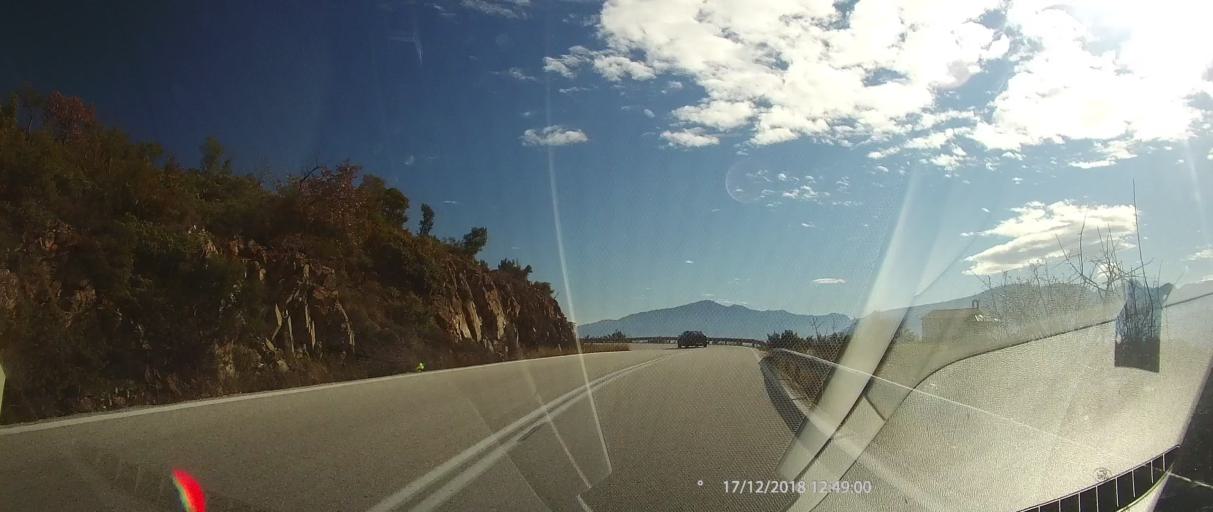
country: GR
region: Thessaly
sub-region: Trikala
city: Kastraki
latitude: 39.7811
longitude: 21.4403
